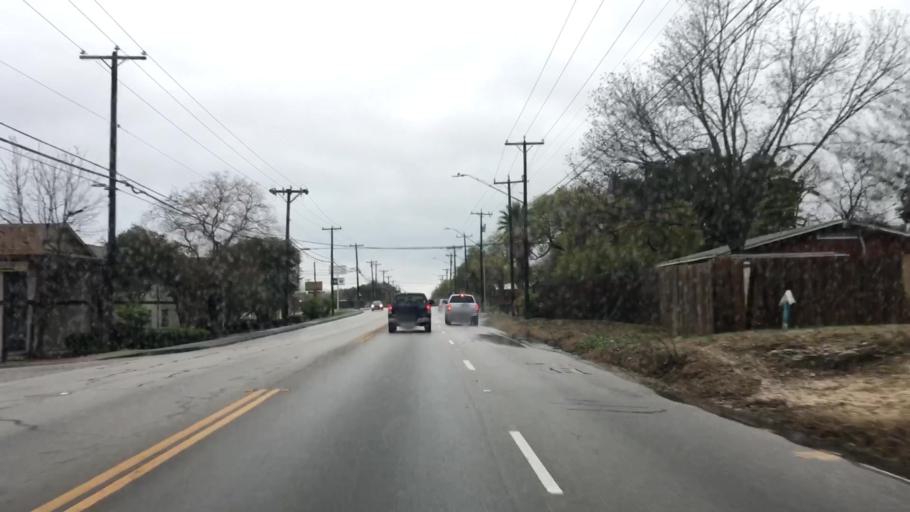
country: US
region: Texas
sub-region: Bexar County
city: Castle Hills
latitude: 29.5119
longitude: -98.5069
